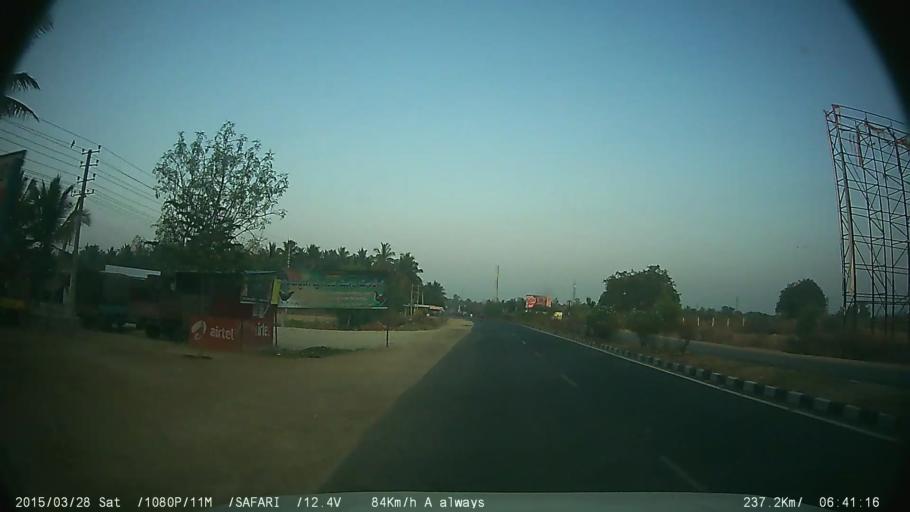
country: IN
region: Karnataka
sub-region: Ramanagara
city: Channapatna
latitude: 12.6404
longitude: 77.1465
